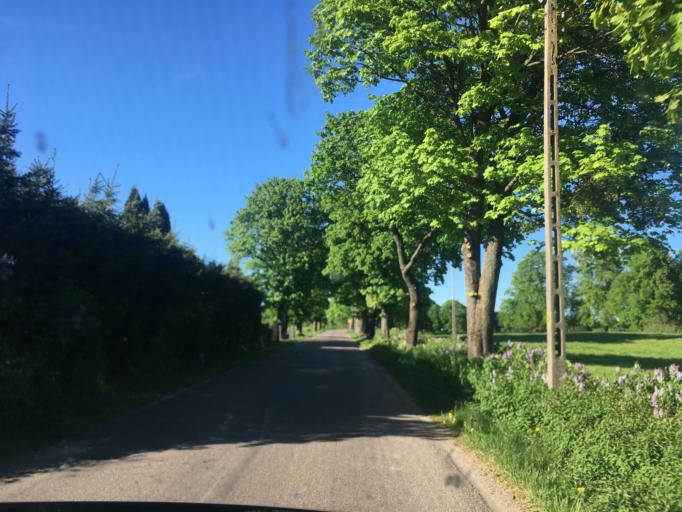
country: PL
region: Warmian-Masurian Voivodeship
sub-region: Powiat piski
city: Ruciane-Nida
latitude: 53.6767
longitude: 21.4933
